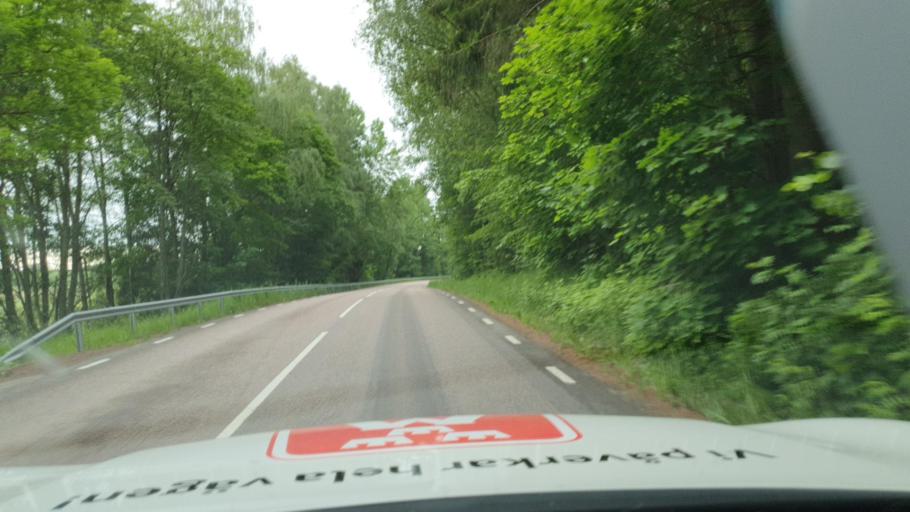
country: SE
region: Vaermland
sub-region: Kils Kommun
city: Kil
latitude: 59.5120
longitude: 13.3896
